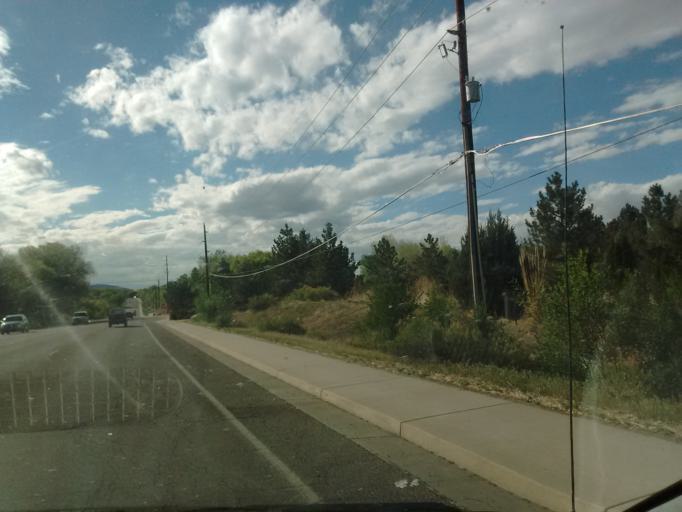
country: US
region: Colorado
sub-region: Mesa County
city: Redlands
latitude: 39.0646
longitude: -108.5957
